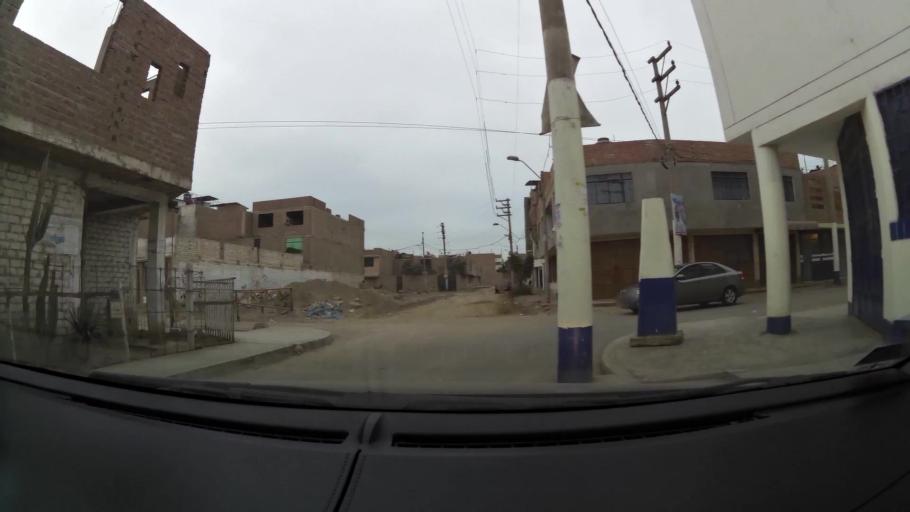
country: PE
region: Lima
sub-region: Lima
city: Independencia
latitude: -11.9749
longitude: -77.0936
